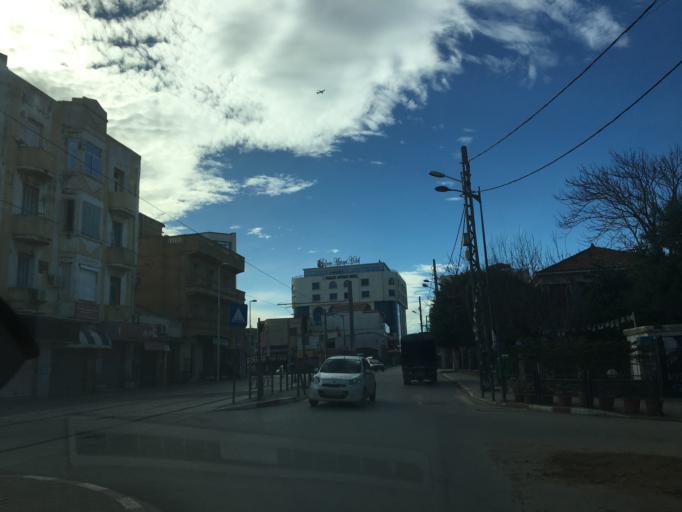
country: DZ
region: Alger
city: Bordj el Kiffan
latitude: 36.7465
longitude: 3.1887
